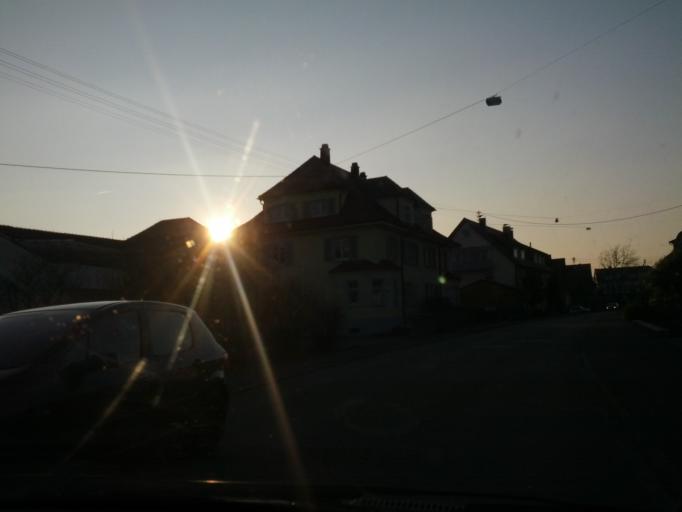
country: DE
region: Baden-Wuerttemberg
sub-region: Freiburg Region
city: Ihringen
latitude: 48.0419
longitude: 7.6532
